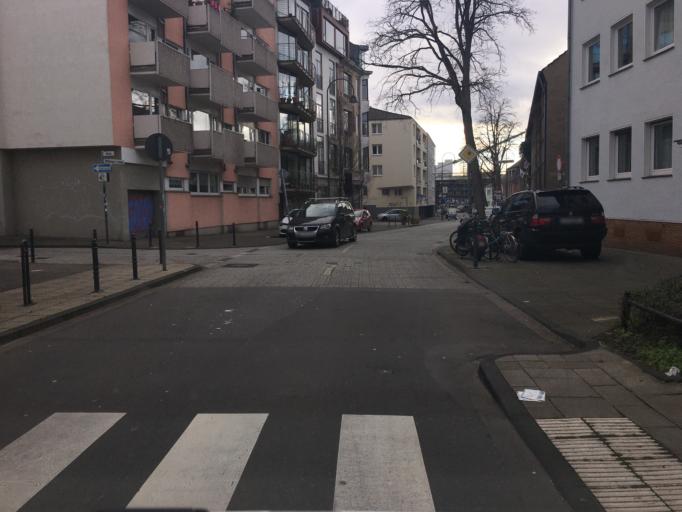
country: DE
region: North Rhine-Westphalia
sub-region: Regierungsbezirk Koln
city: Muelheim
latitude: 50.9650
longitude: 7.0004
